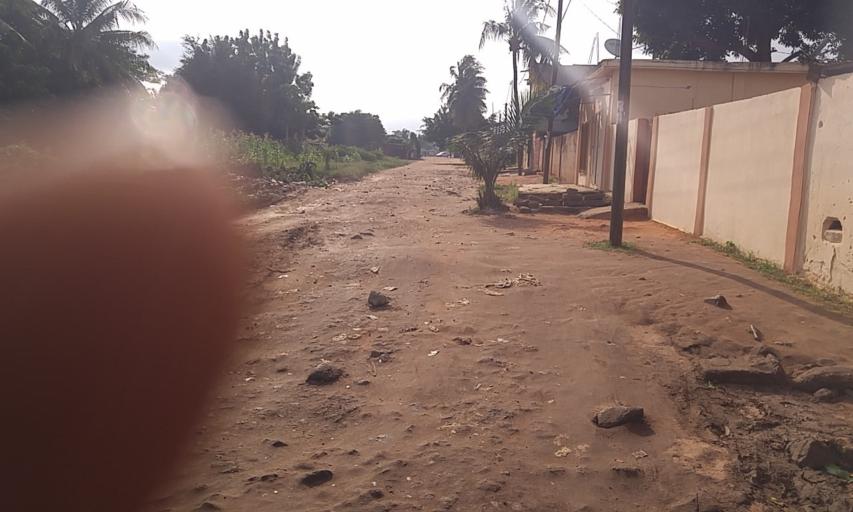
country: TG
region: Maritime
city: Lome
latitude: 6.1790
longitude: 1.1876
